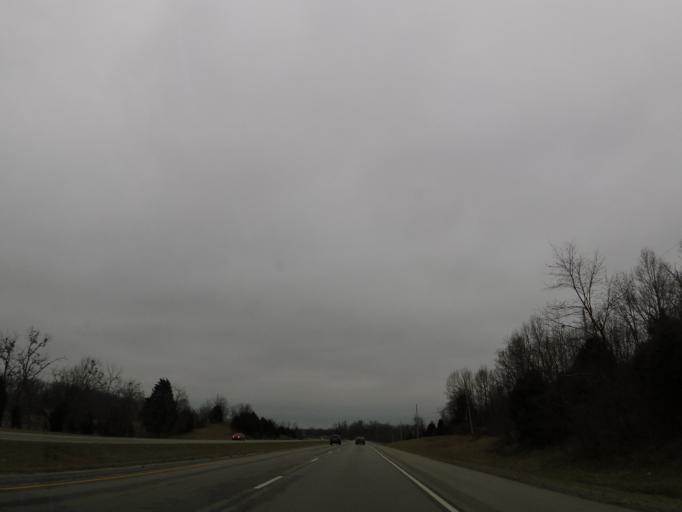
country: US
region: Kentucky
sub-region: Franklin County
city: Frankfort
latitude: 38.1264
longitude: -84.9151
